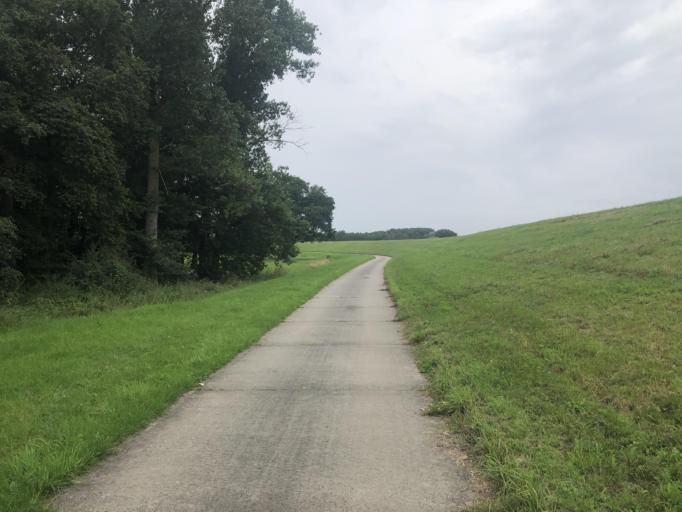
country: DE
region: Mecklenburg-Vorpommern
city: Nostorf
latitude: 53.3618
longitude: 10.6703
